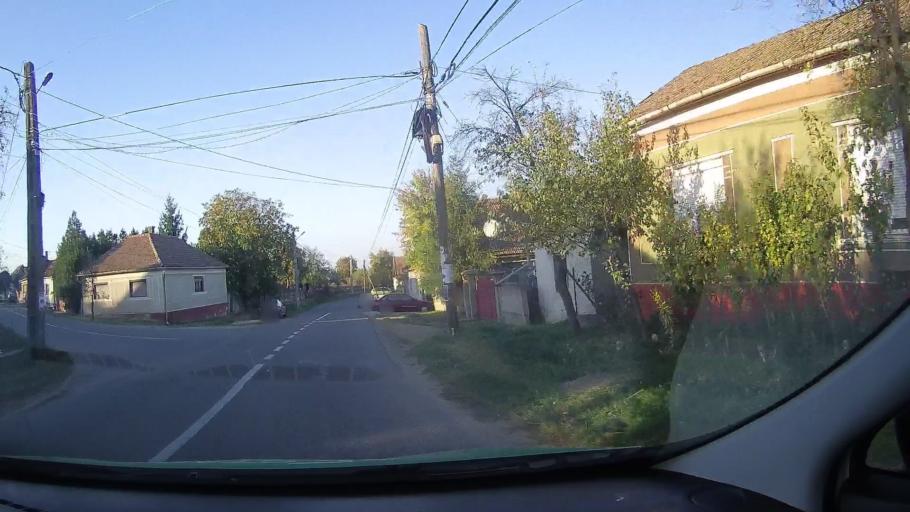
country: RO
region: Bihor
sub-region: Comuna Cetariu
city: Cetariu
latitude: 47.1464
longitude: 22.0003
